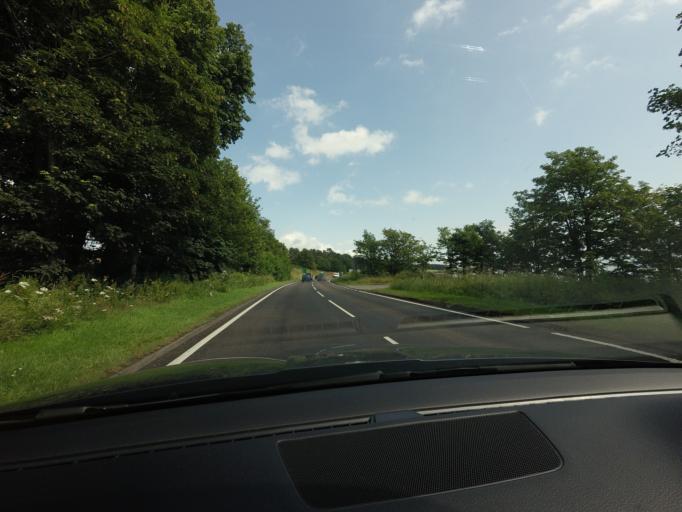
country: GB
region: Scotland
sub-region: Highland
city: Evanton
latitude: 57.6287
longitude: -4.3672
